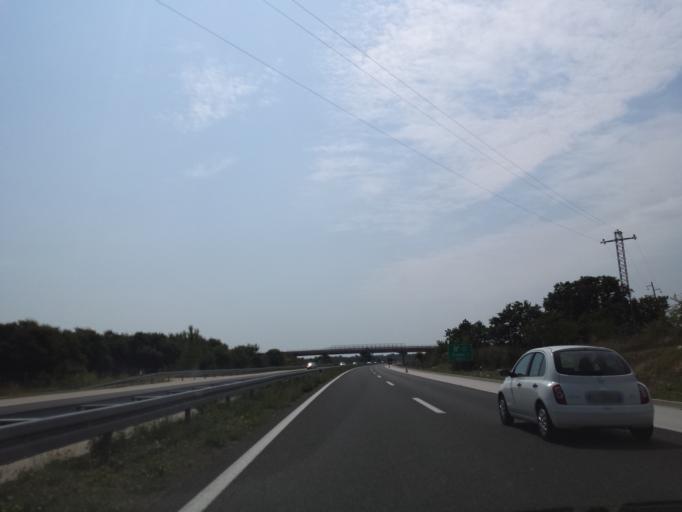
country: HR
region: Zadarska
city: Posedarje
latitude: 44.2040
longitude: 15.4441
